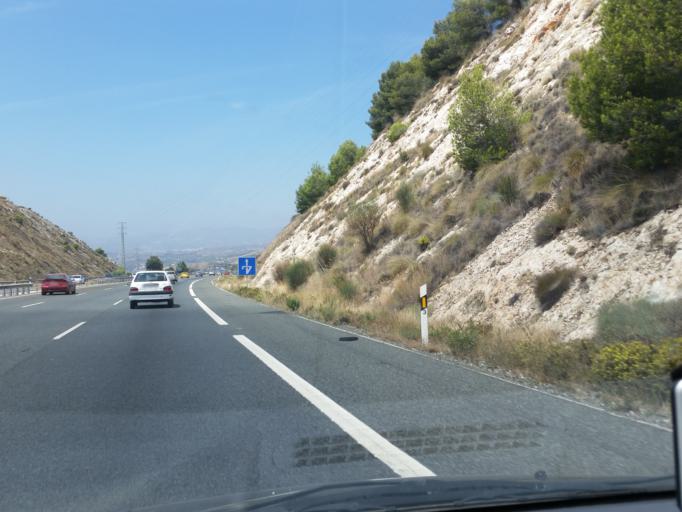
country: ES
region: Andalusia
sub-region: Provincia de Malaga
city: Benalmadena
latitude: 36.5888
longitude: -4.5860
